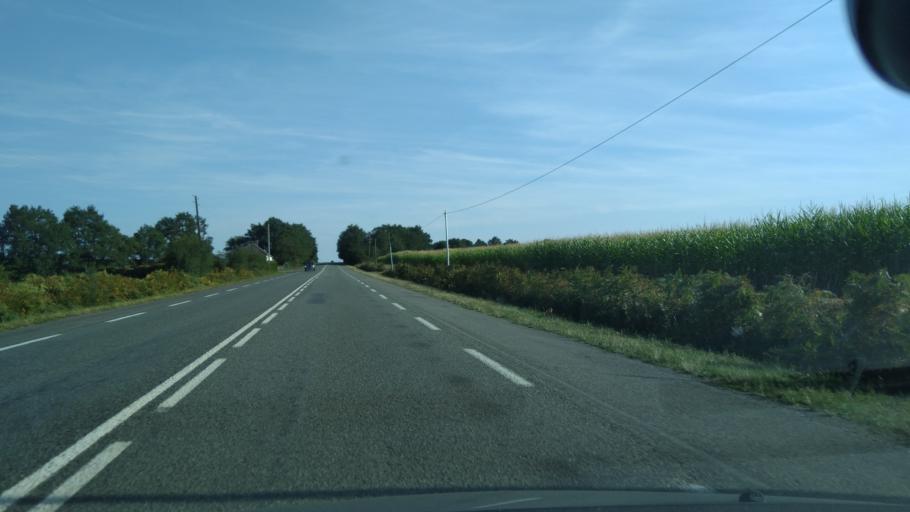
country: FR
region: Pays de la Loire
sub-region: Departement de la Mayenne
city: Entrammes
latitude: 47.9536
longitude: -0.7014
